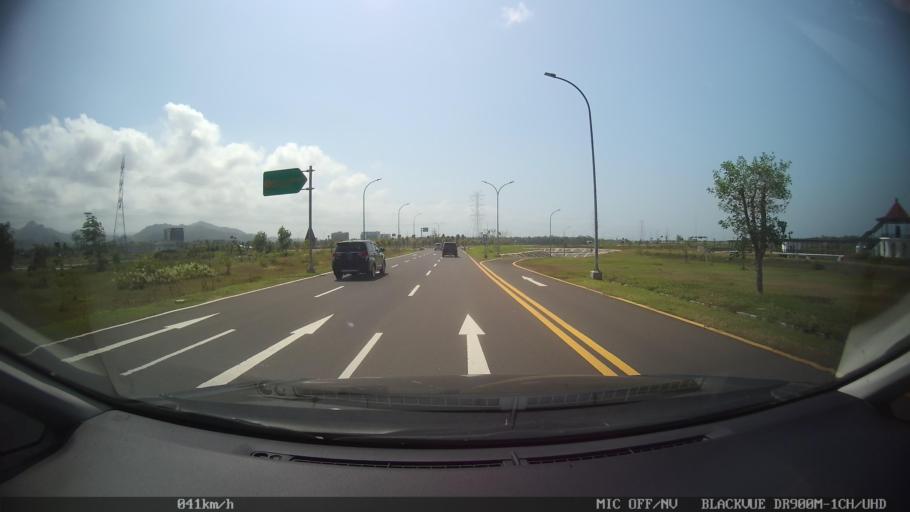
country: ID
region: Daerah Istimewa Yogyakarta
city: Srandakan
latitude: -7.8922
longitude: 110.0599
